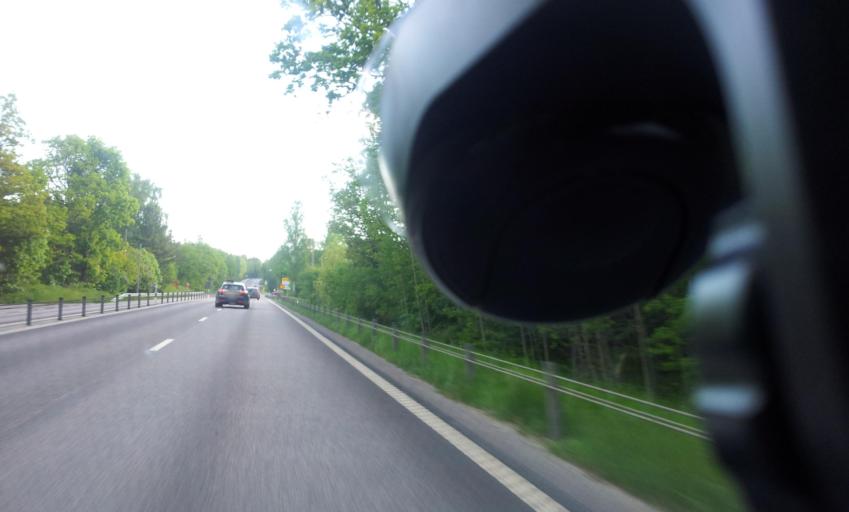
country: SE
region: Kalmar
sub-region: Oskarshamns Kommun
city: Oskarshamn
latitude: 57.3034
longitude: 16.4616
